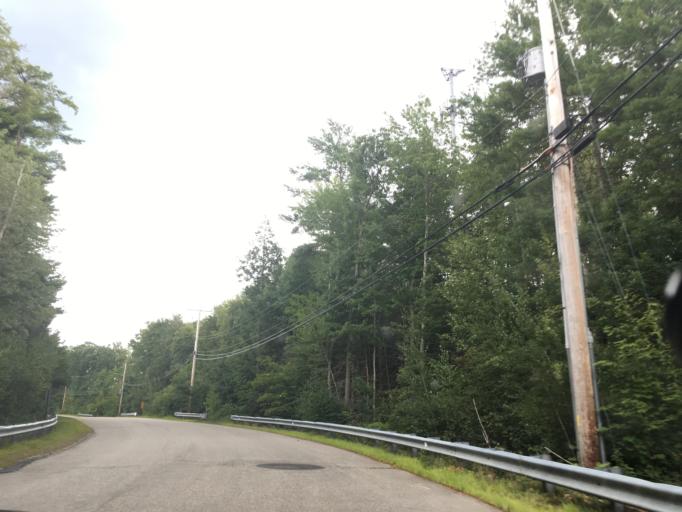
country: US
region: New Hampshire
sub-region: Rockingham County
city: Exeter
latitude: 42.9947
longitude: -70.9778
